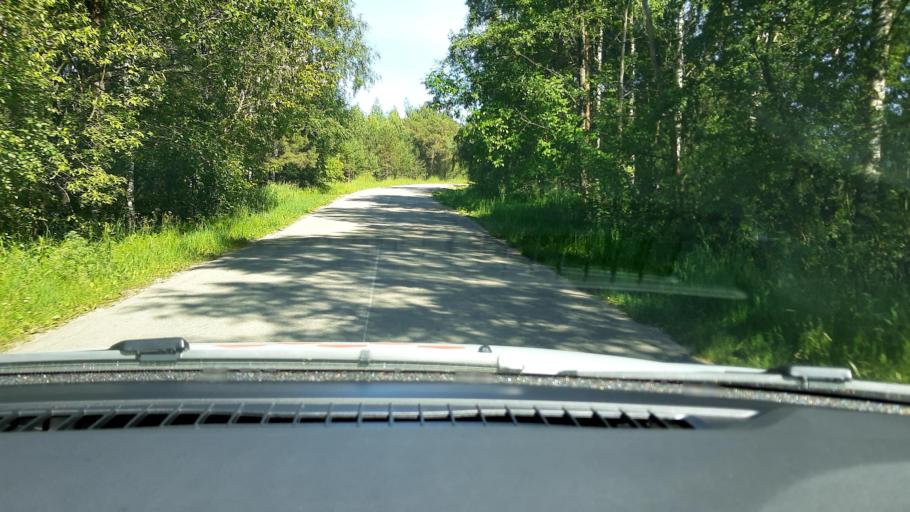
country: RU
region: Nizjnij Novgorod
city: Sitniki
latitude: 56.5249
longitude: 44.1234
